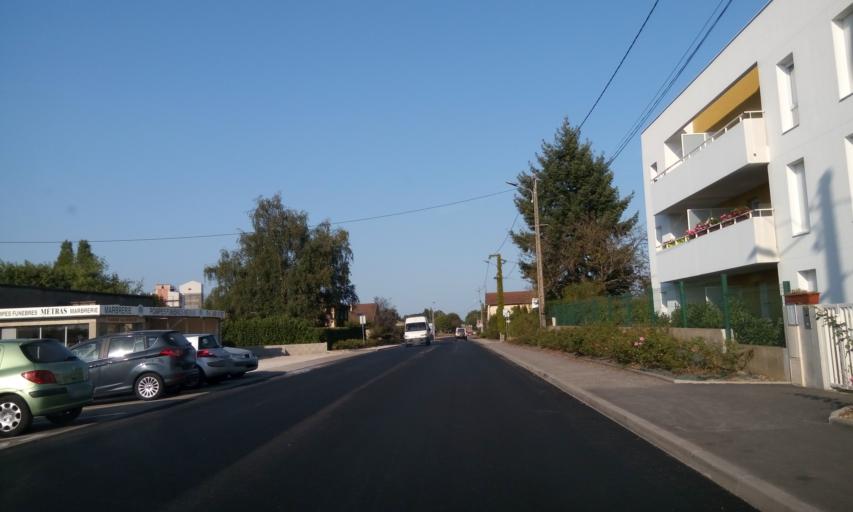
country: FR
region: Rhone-Alpes
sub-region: Departement de l'Ain
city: Villars-les-Dombes
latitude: 46.0053
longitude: 5.0315
